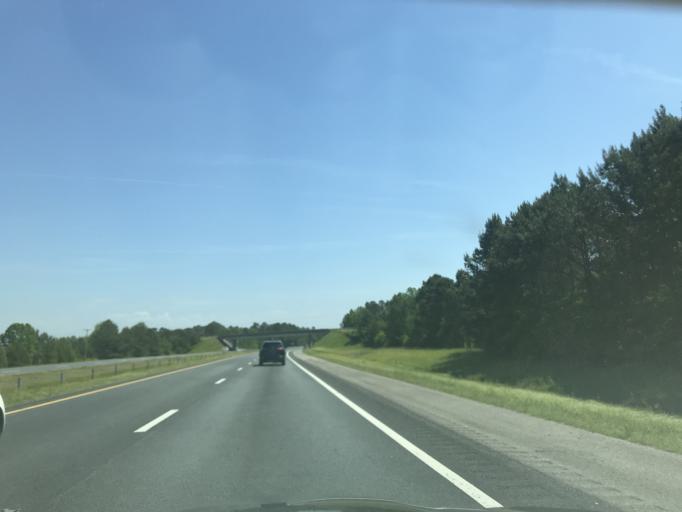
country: US
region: North Carolina
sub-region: Johnston County
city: Benson
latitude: 35.3688
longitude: -78.4960
